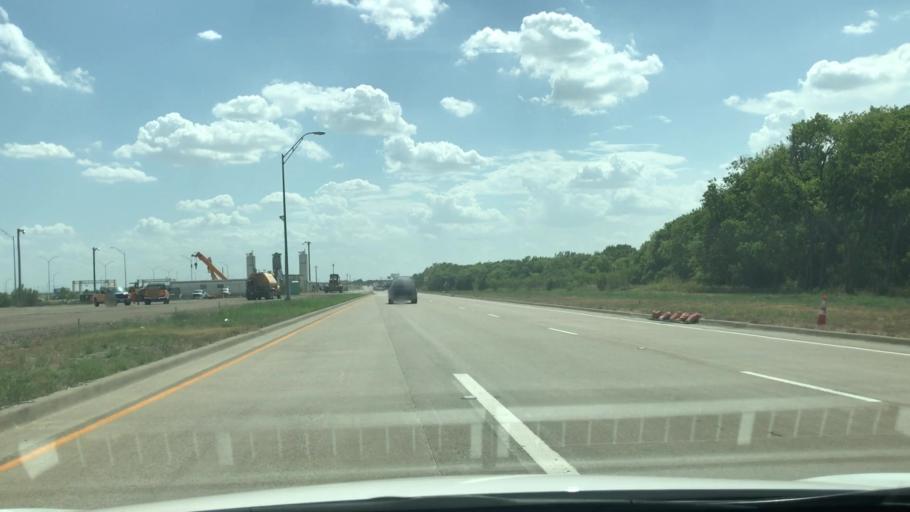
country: US
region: Texas
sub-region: Tarrant County
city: Grapevine
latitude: 32.9297
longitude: -97.0513
